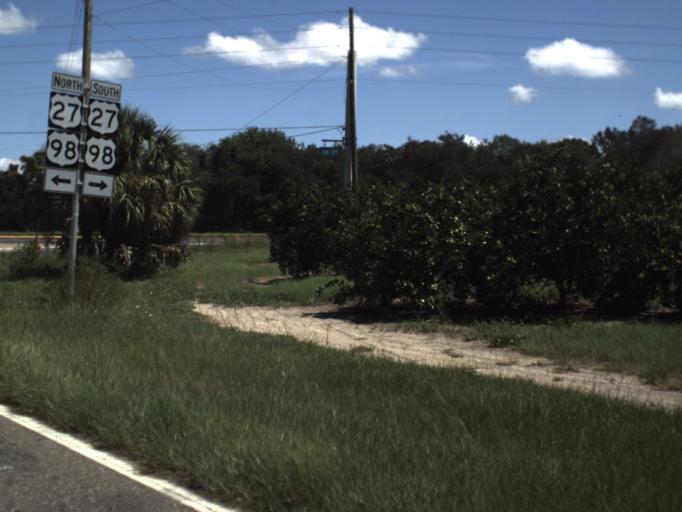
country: US
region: Florida
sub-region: Polk County
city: Frostproof
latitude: 27.6770
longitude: -81.5541
